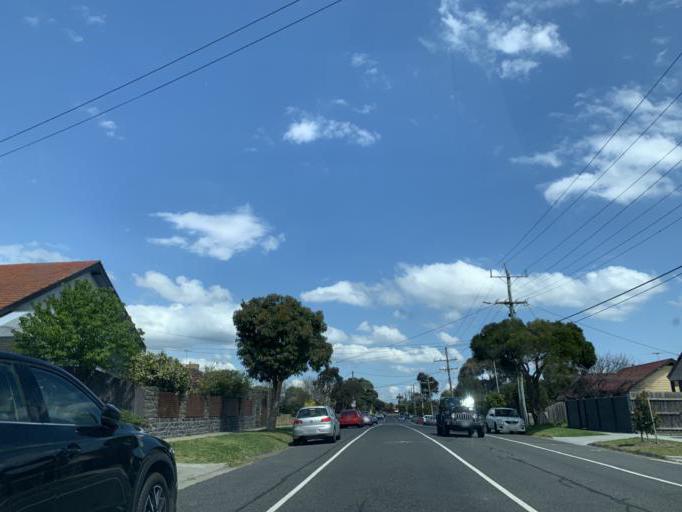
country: AU
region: Victoria
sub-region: Kingston
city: Mordialloc
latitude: -38.0060
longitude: 145.0928
